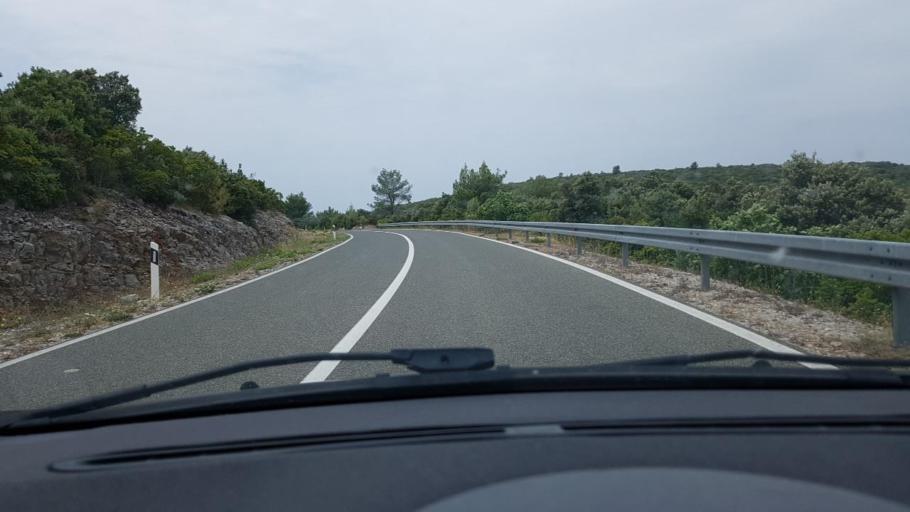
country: HR
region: Dubrovacko-Neretvanska
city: Smokvica
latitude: 42.9491
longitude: 16.9510
